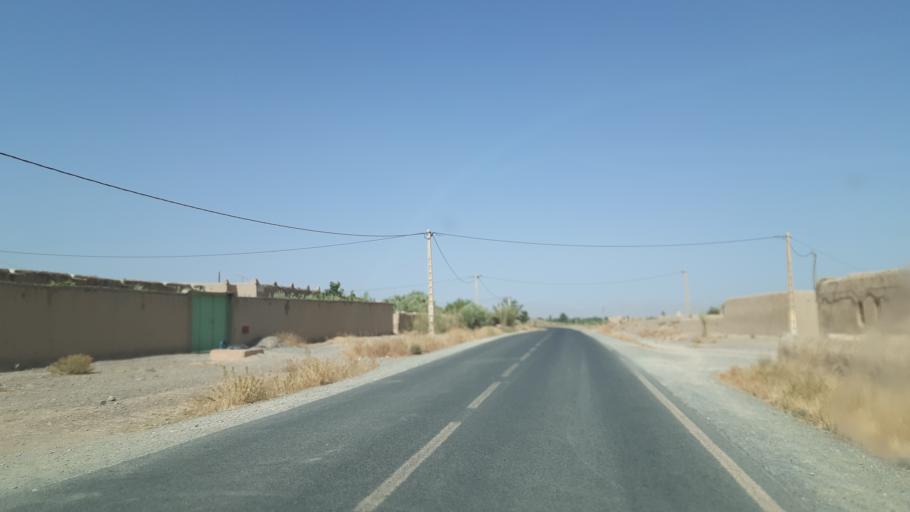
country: MA
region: Meknes-Tafilalet
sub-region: Errachidia
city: Errachidia
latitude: 32.2520
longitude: -4.5750
